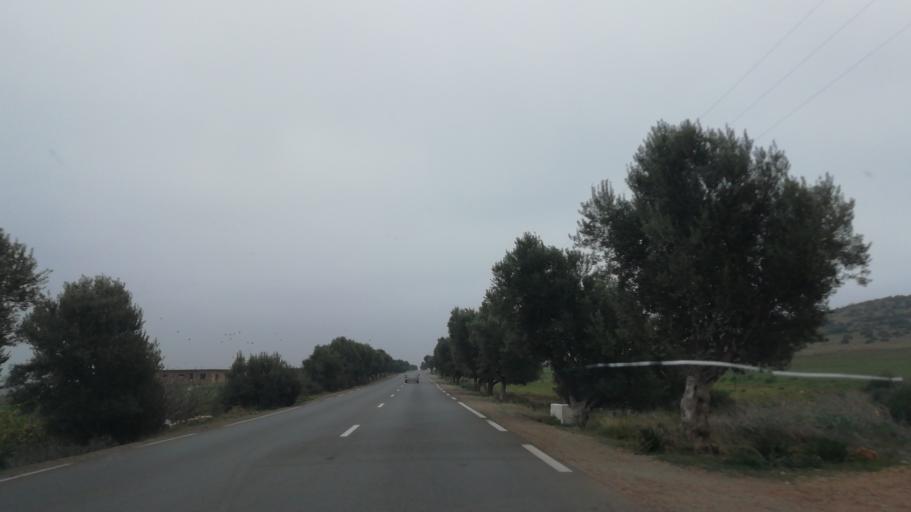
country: DZ
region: Mascara
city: Mascara
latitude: 35.3103
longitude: 0.3994
